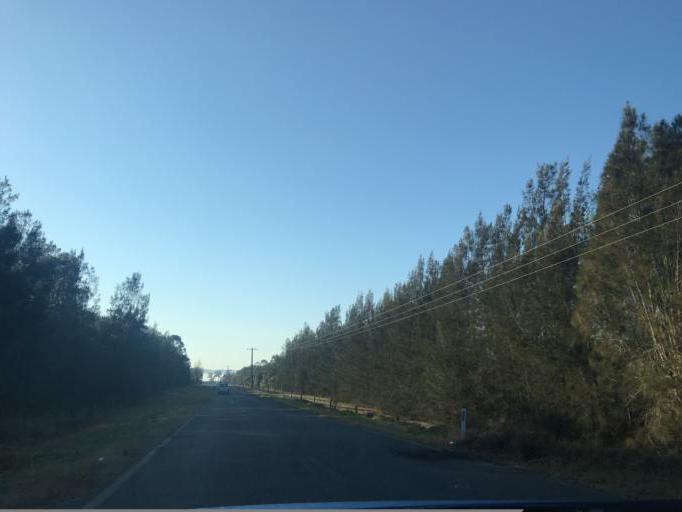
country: AU
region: New South Wales
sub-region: Cessnock
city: Cessnock
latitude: -32.9075
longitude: 151.2900
